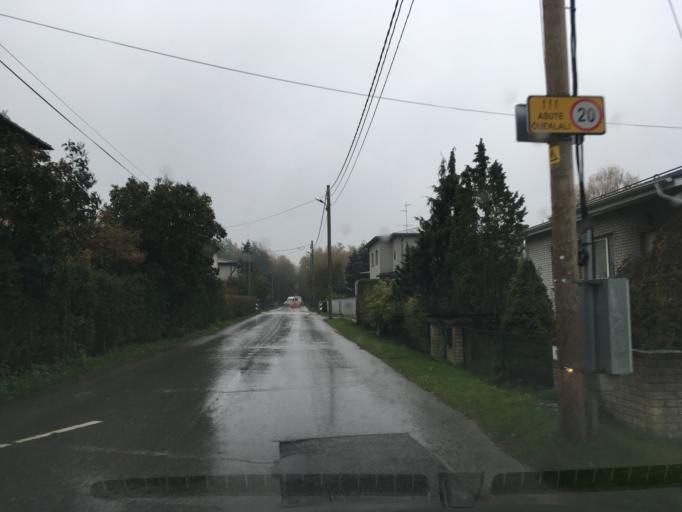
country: EE
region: Harju
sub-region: Tallinna linn
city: Kose
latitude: 59.4560
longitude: 24.8511
